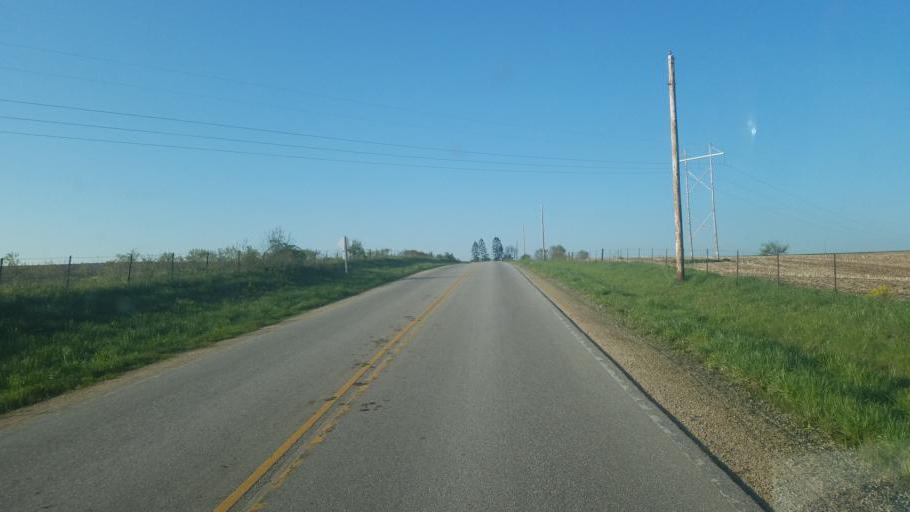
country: US
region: Wisconsin
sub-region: Vernon County
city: Hillsboro
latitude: 43.5714
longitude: -90.5154
